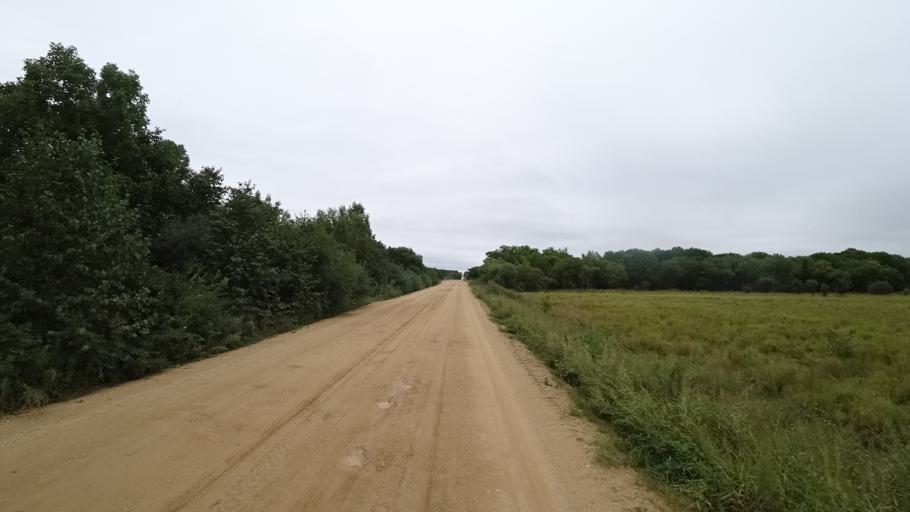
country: RU
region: Primorskiy
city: Ivanovka
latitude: 44.0654
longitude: 132.5729
